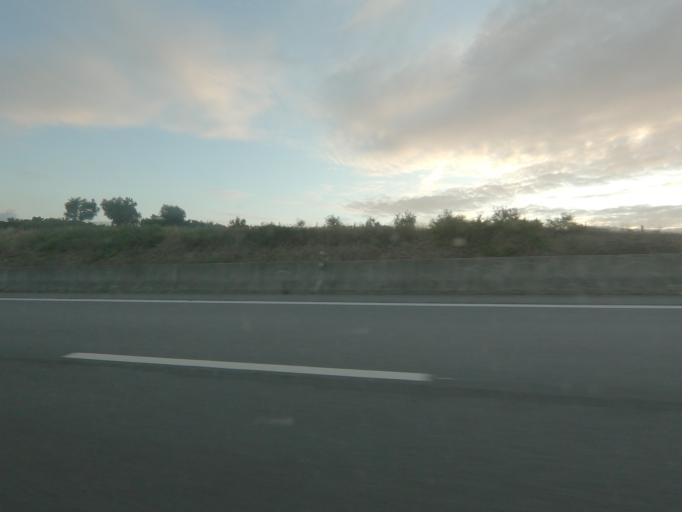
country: PT
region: Vila Real
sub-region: Peso da Regua
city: Peso da Regua
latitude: 41.1937
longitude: -7.7508
